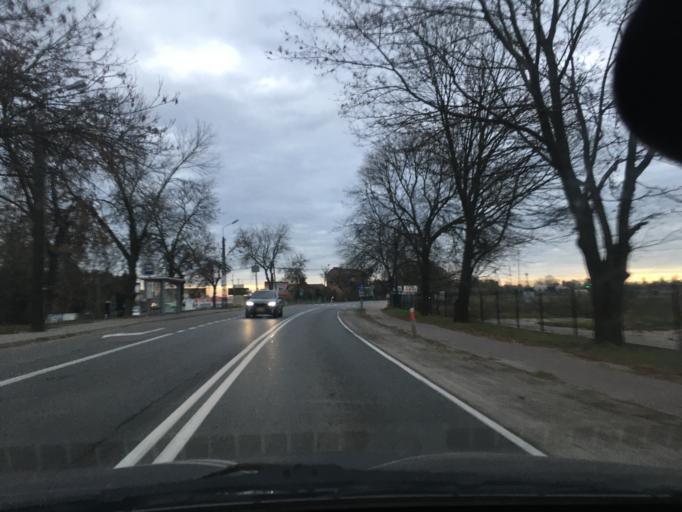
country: PL
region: Masovian Voivodeship
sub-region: Powiat piaseczynski
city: Lesznowola
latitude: 52.0960
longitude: 20.9229
